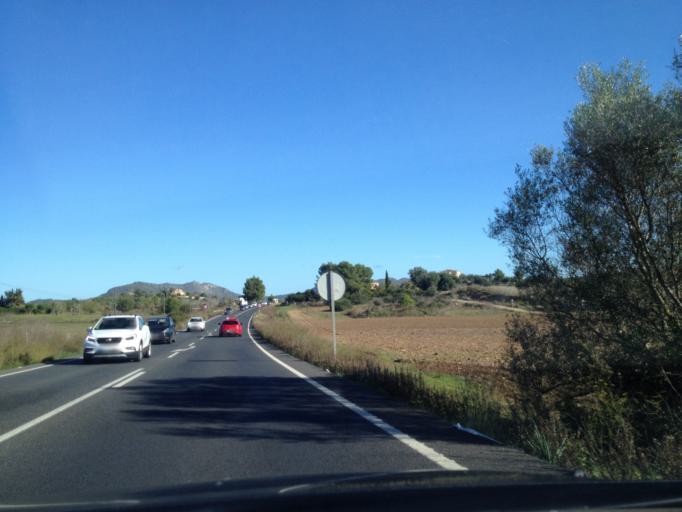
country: ES
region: Balearic Islands
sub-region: Illes Balears
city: Sant Llorenc des Cardassar
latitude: 39.5974
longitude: 3.2674
